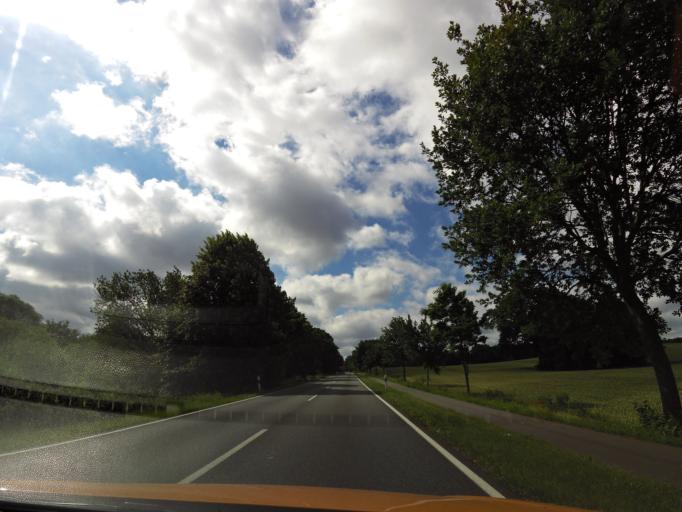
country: DE
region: Mecklenburg-Vorpommern
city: Krakow am See
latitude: 53.6813
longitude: 12.2678
